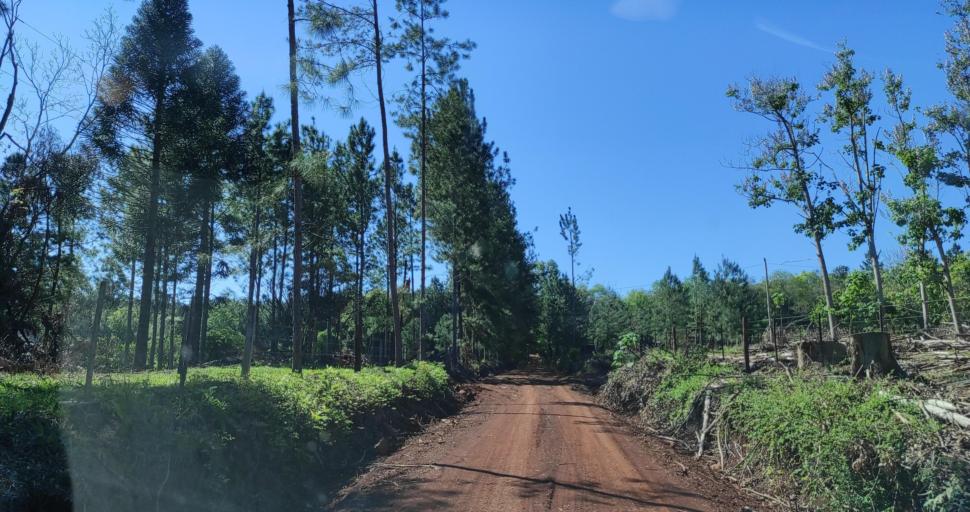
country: AR
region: Misiones
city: Ruiz de Montoya
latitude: -26.9473
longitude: -55.0029
